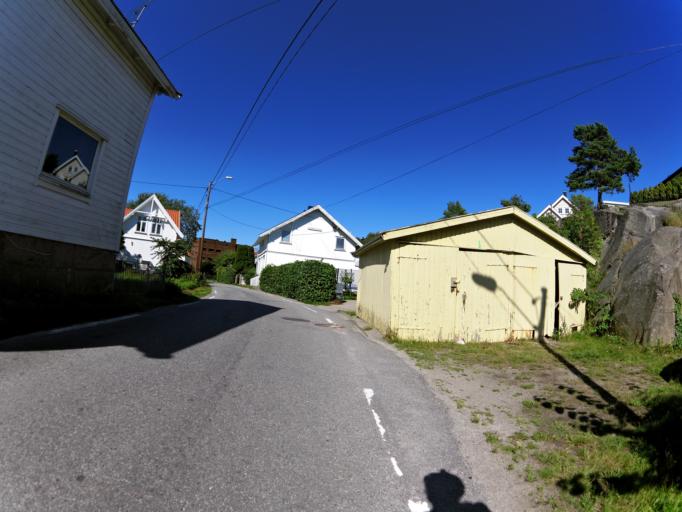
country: NO
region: Ostfold
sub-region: Fredrikstad
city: Fredrikstad
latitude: 59.1723
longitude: 10.8502
